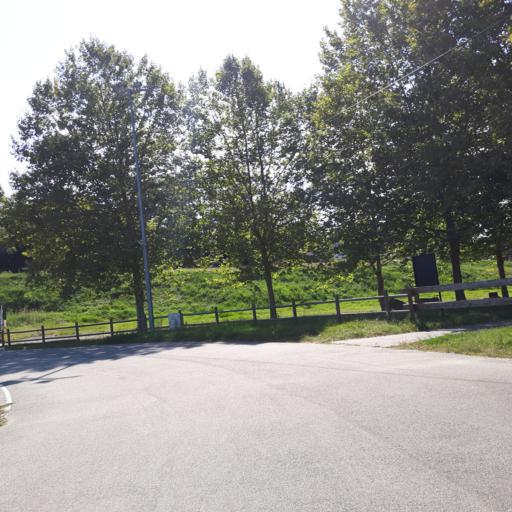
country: FR
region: Midi-Pyrenees
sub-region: Departement de la Haute-Garonne
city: Grenade
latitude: 43.7751
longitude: 1.2951
